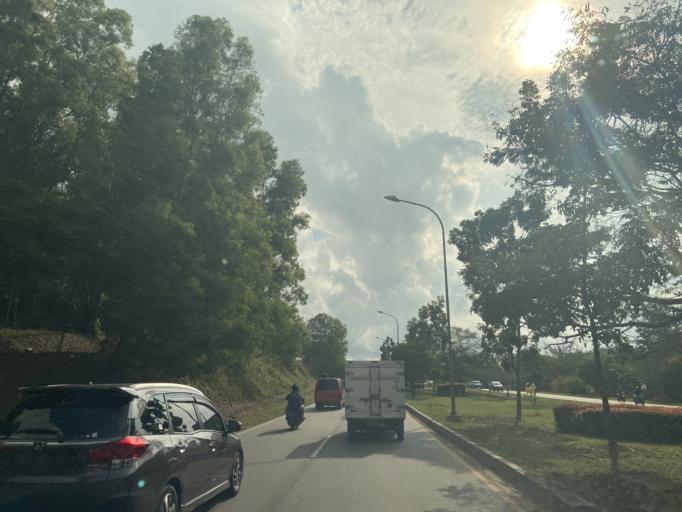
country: SG
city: Singapore
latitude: 1.0988
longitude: 104.0629
